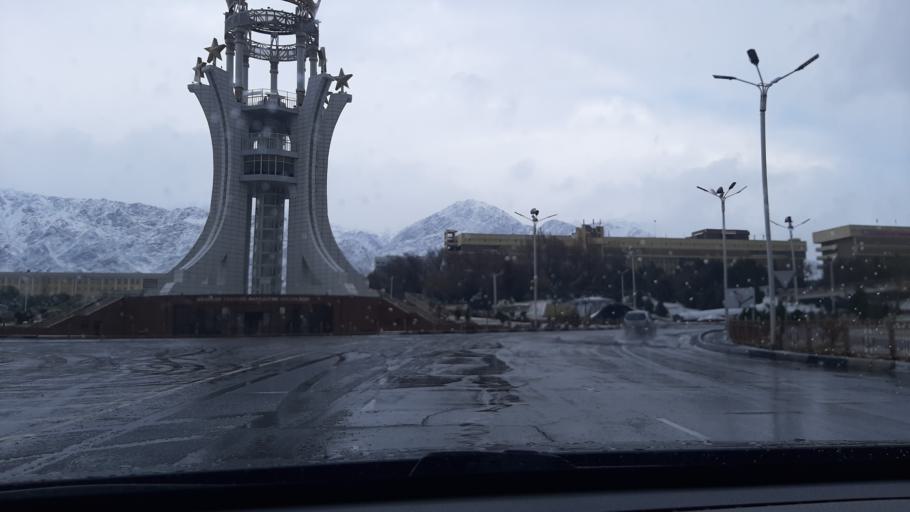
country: TJ
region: Viloyati Sughd
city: Khujand
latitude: 40.3012
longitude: 69.6144
